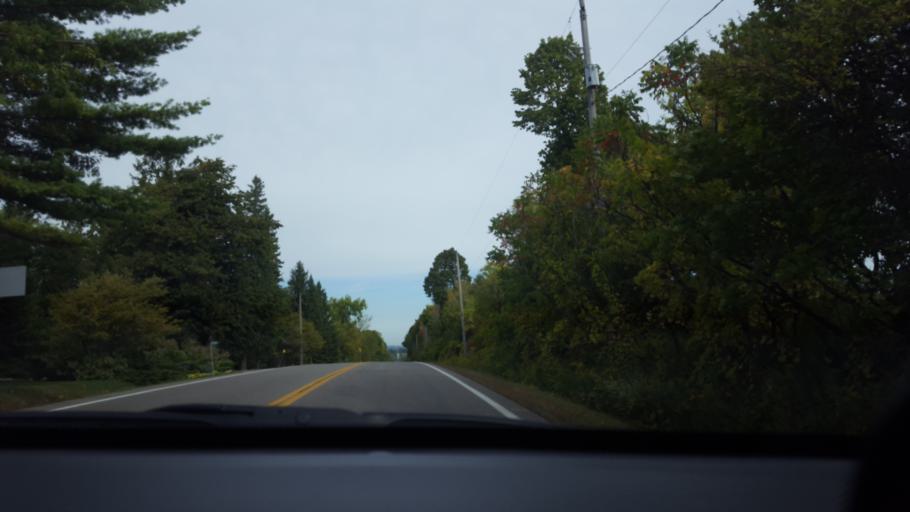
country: CA
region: Ontario
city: Newmarket
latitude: 43.9840
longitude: -79.5433
